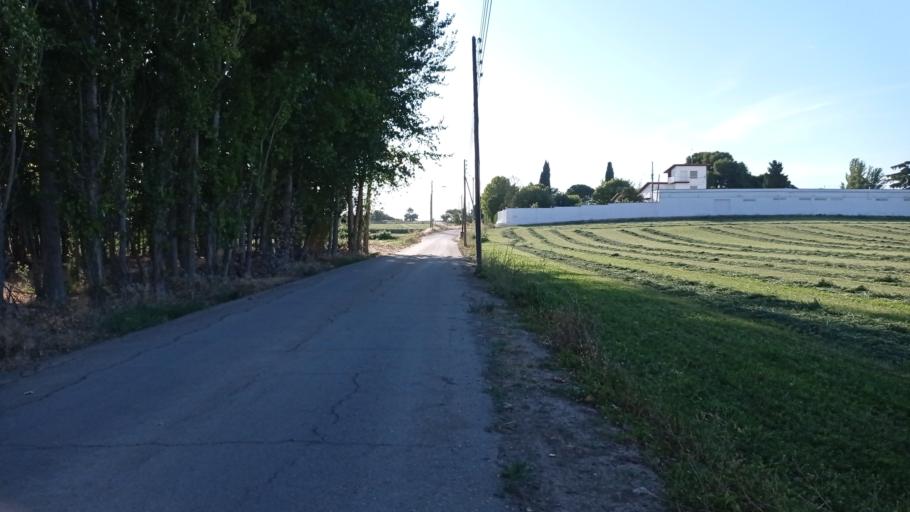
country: ES
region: Aragon
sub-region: Provincia de Zaragoza
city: Oliver-Valdefierro, Oliver, Valdefierro
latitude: 41.6652
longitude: -0.9596
